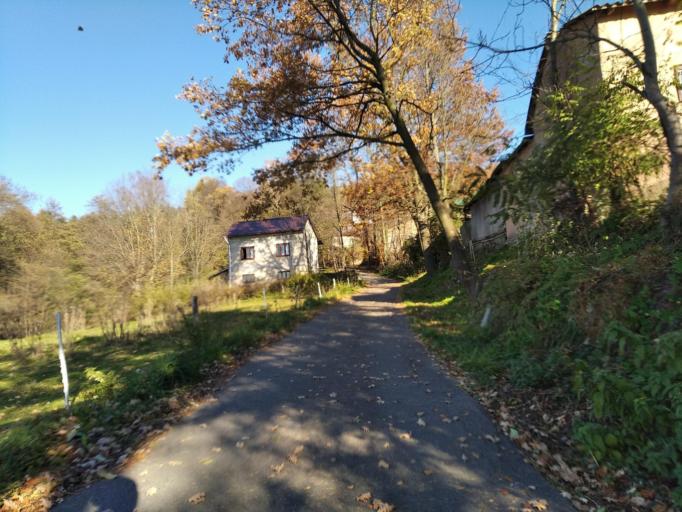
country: PL
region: Subcarpathian Voivodeship
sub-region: Powiat strzyzowski
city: Frysztak
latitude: 49.8511
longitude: 21.6121
